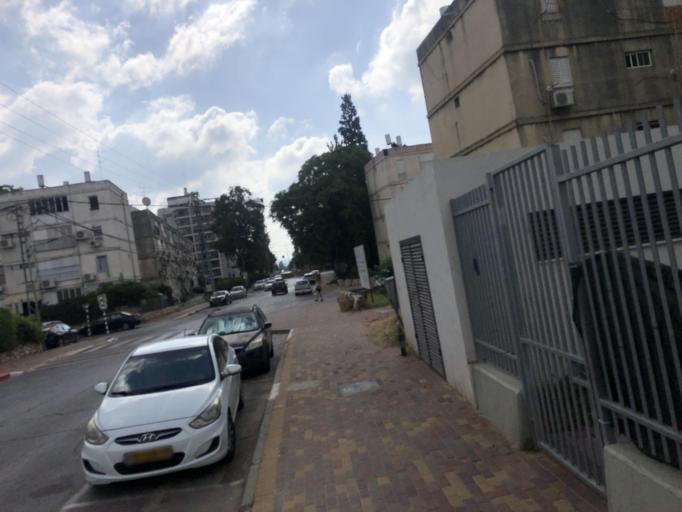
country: IL
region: Central District
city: Yehud
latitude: 32.0343
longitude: 34.8911
